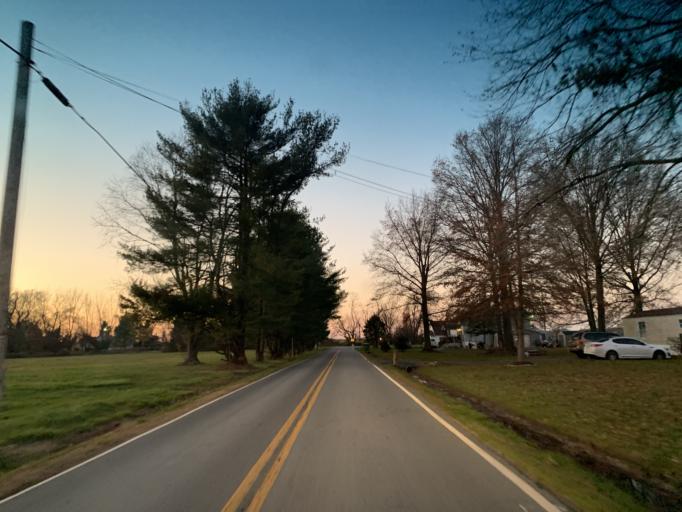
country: US
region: Delaware
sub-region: New Castle County
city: Middletown
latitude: 39.4208
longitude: -75.7780
